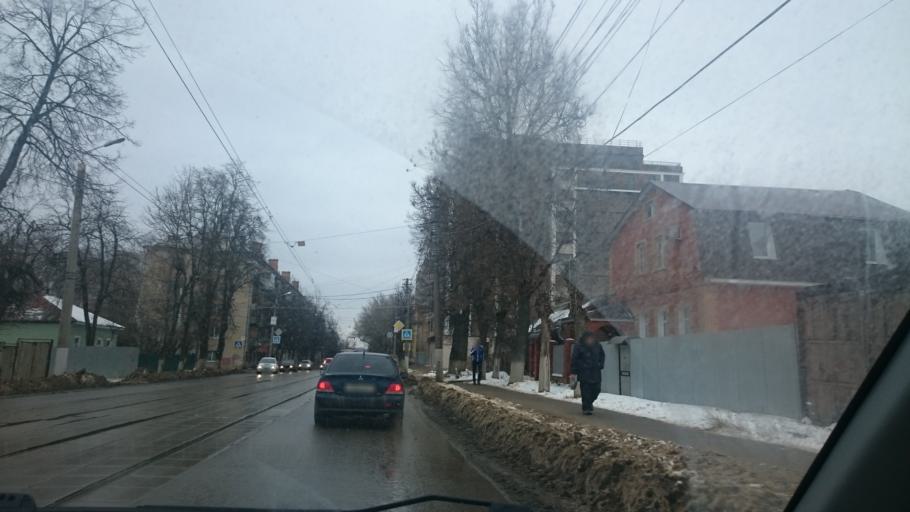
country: RU
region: Tula
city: Mendeleyevskiy
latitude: 54.1658
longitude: 37.5957
